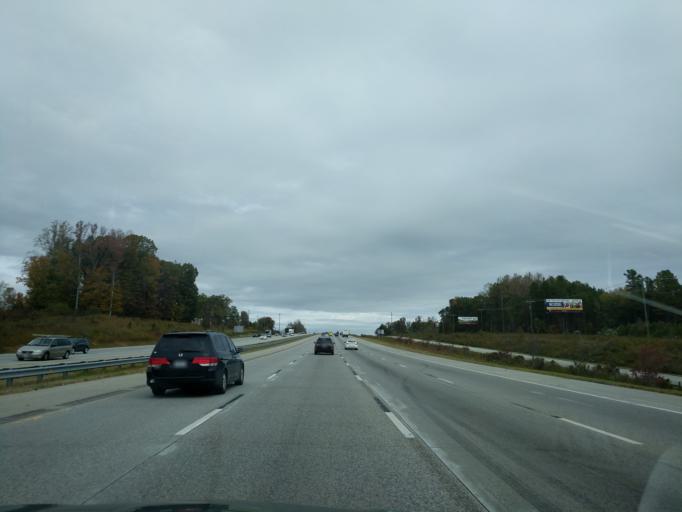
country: US
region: North Carolina
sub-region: Rowan County
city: Spencer
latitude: 35.7024
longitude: -80.3986
